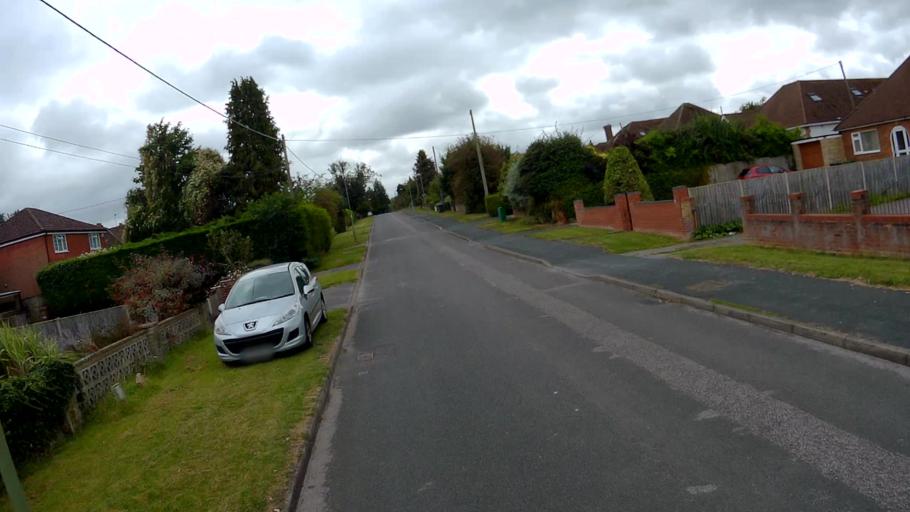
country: GB
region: England
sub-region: Hampshire
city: Basingstoke
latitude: 51.2548
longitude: -1.1381
